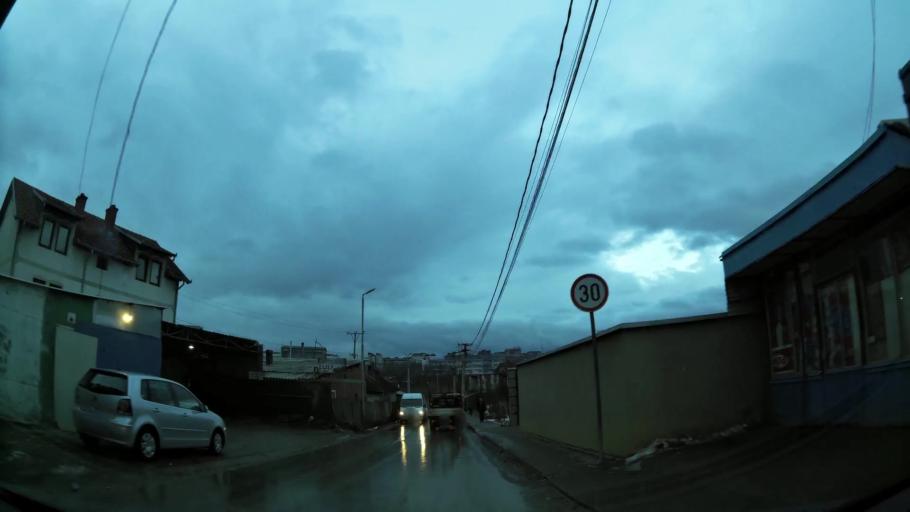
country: XK
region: Pristina
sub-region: Komuna e Prishtines
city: Pristina
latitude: 42.6402
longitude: 21.1635
